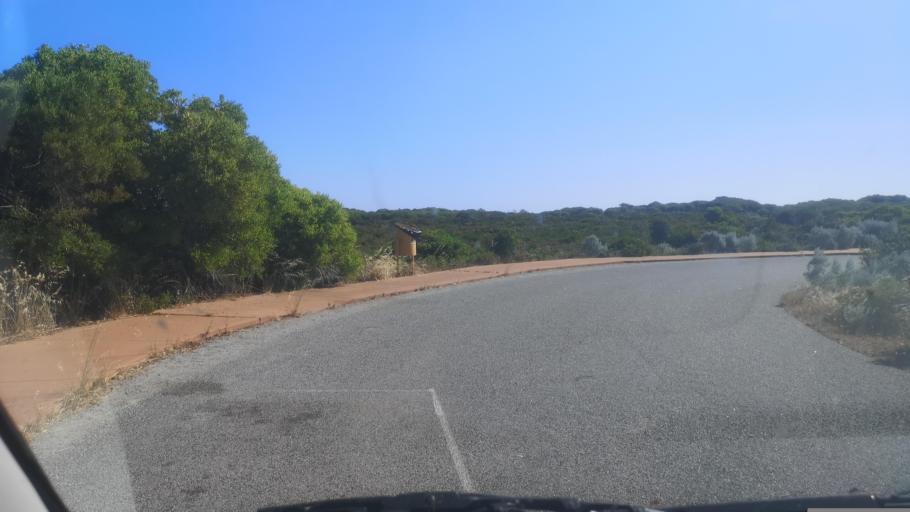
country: AU
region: Western Australia
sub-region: Dandaragan
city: Jurien Bay
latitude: -30.7915
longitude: 115.2259
